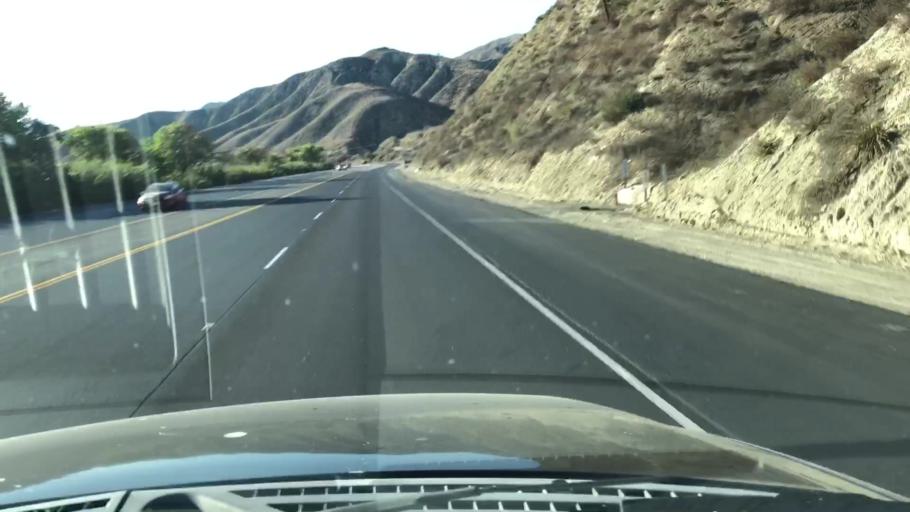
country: US
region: California
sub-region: Ventura County
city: Piru
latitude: 34.4072
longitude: -118.7220
